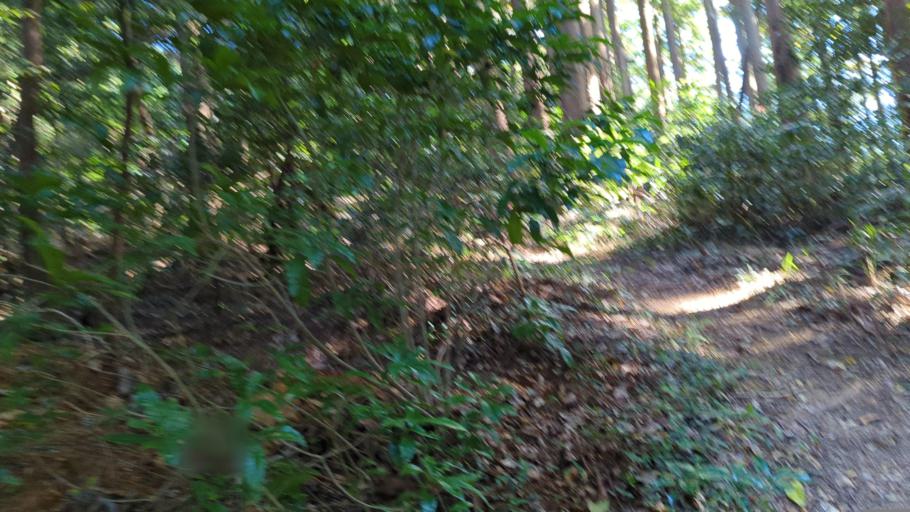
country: JP
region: Aichi
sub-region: Tokai-shi
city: Toyokawa
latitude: 34.7717
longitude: 137.4644
